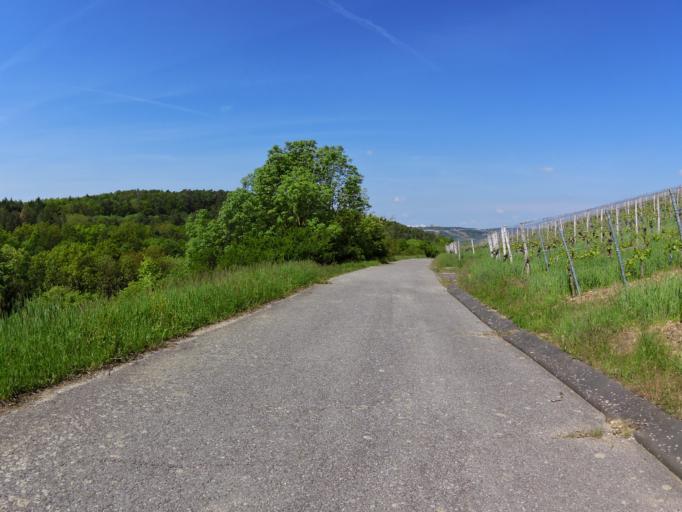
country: DE
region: Bavaria
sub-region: Regierungsbezirk Unterfranken
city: Eibelstadt
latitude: 49.7317
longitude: 10.0185
